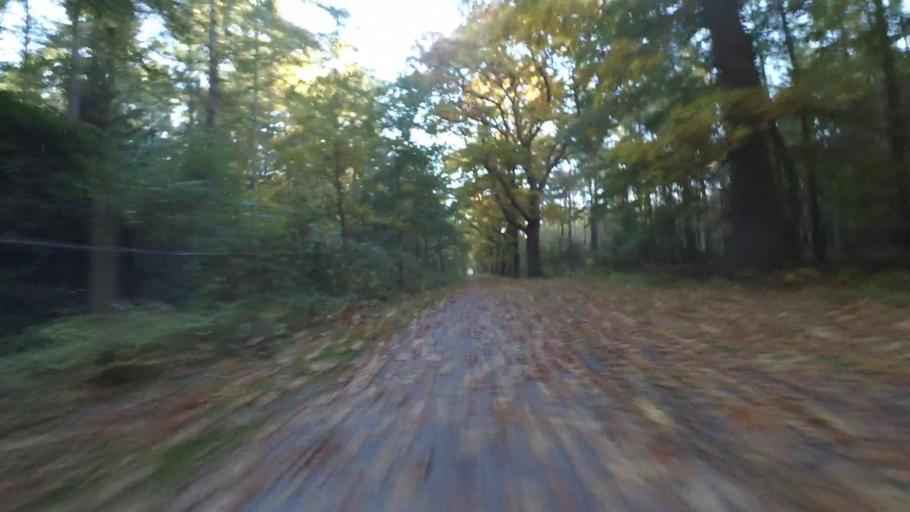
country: NL
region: Utrecht
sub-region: Gemeente De Bilt
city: De Bilt
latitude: 52.1516
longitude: 5.2135
